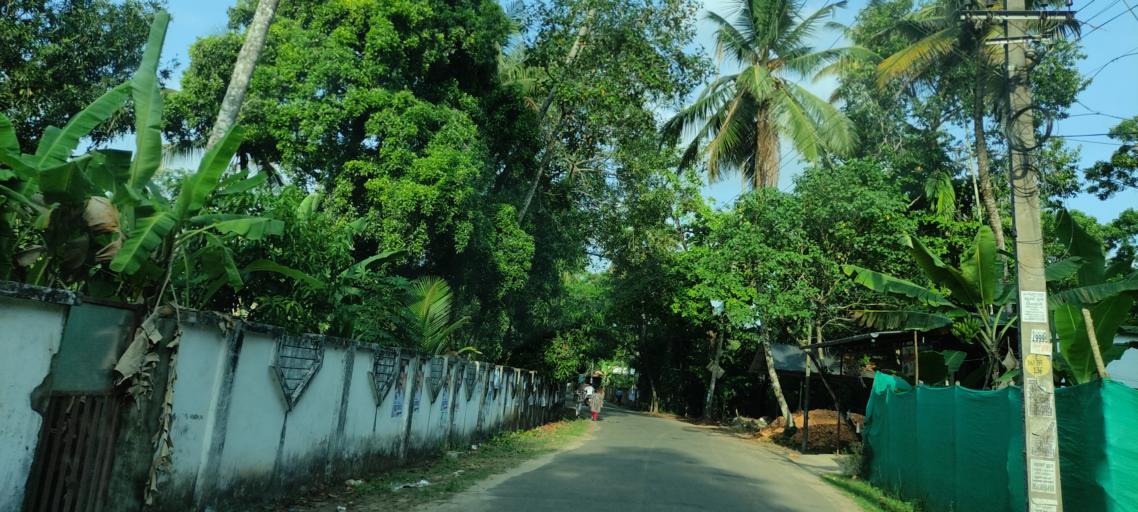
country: IN
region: Kerala
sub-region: Alappuzha
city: Vayalar
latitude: 9.7276
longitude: 76.2915
